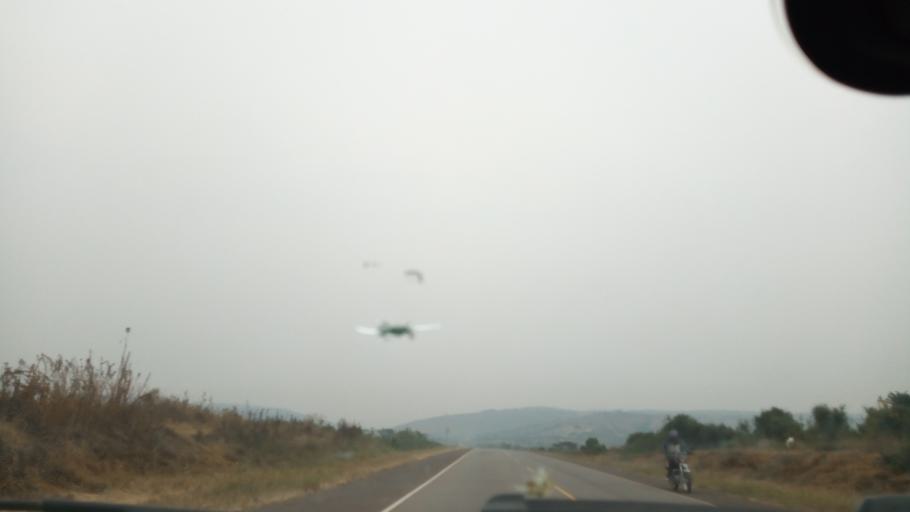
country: UG
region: Western Region
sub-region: Isingiro District
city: Isingiro
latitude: -0.7437
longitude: 30.7533
